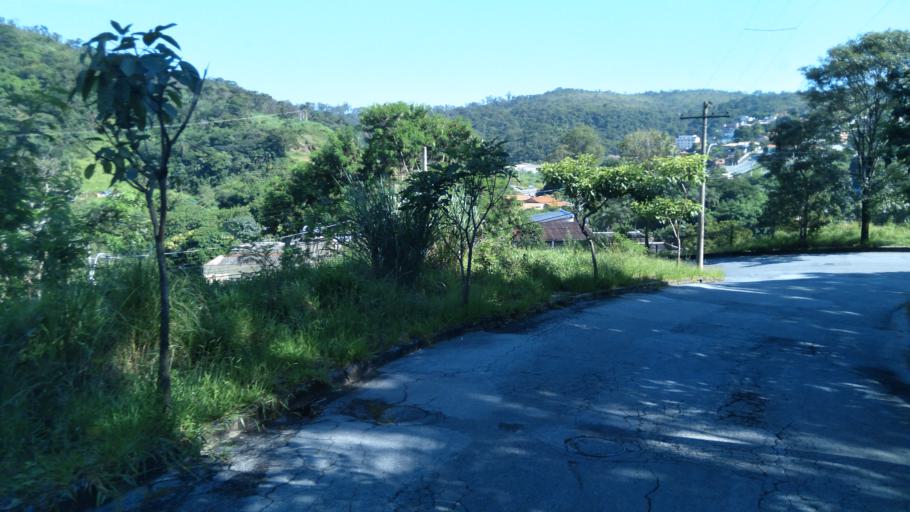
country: BR
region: Minas Gerais
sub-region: Santa Luzia
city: Santa Luzia
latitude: -19.8261
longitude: -43.9032
